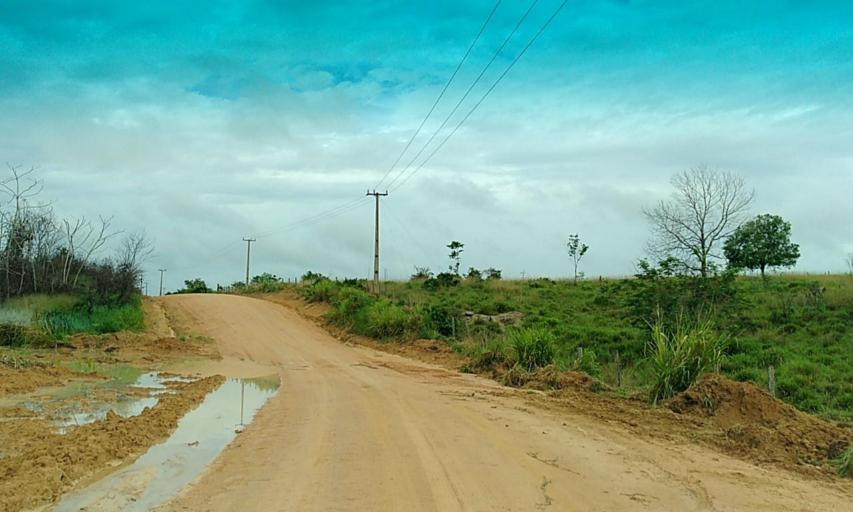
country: BR
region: Para
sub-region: Senador Jose Porfirio
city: Senador Jose Porfirio
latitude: -3.0405
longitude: -51.6782
